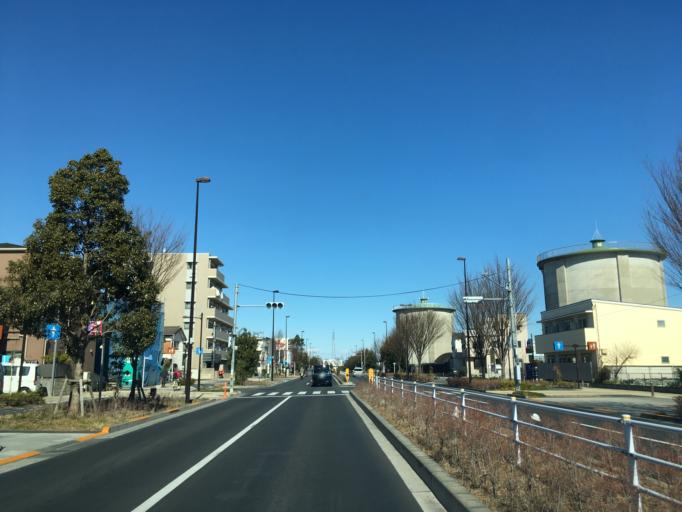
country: JP
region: Tokyo
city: Mitaka-shi
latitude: 35.6856
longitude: 139.5499
